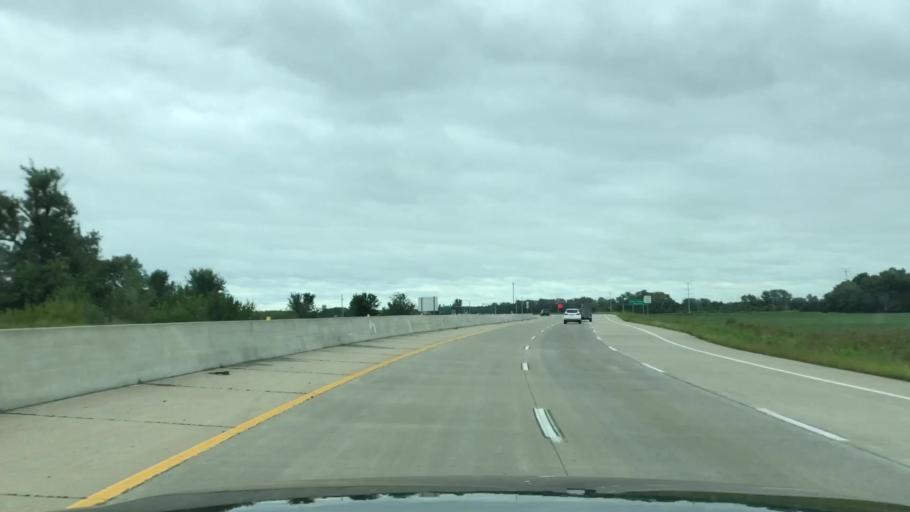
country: US
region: Missouri
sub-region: Saint Louis County
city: Maryland Heights
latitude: 38.7127
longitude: -90.5009
